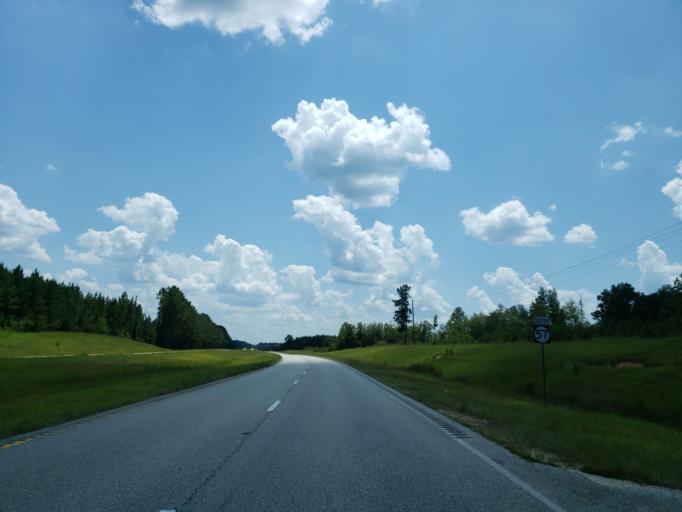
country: US
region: Mississippi
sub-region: Wayne County
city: Belmont
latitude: 31.3908
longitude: -88.4783
